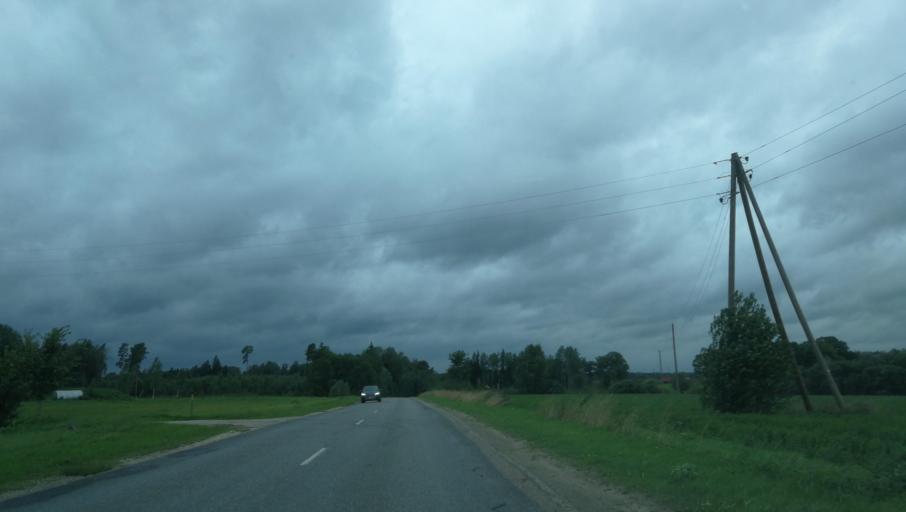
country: LV
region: Beverina
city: Murmuiza
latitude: 57.4803
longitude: 25.4723
